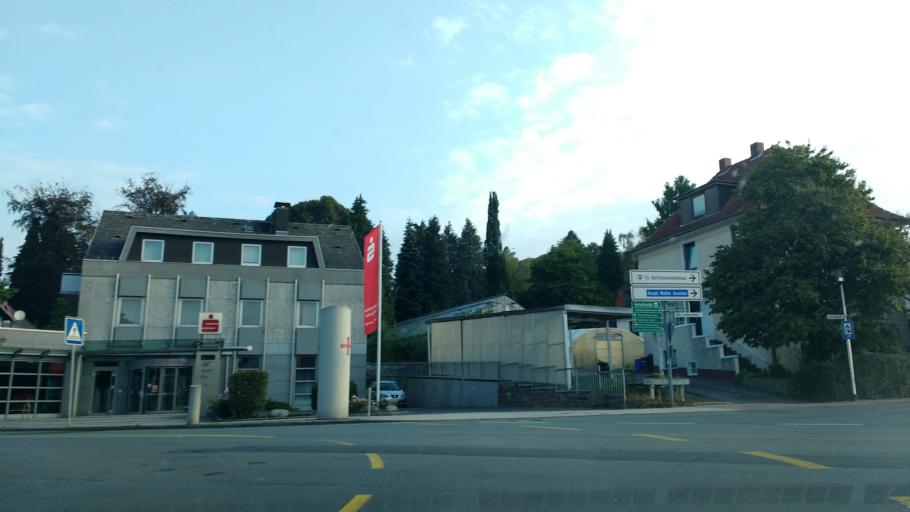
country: DE
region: Lower Saxony
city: Bad Pyrmont
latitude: 51.9843
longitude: 9.2666
